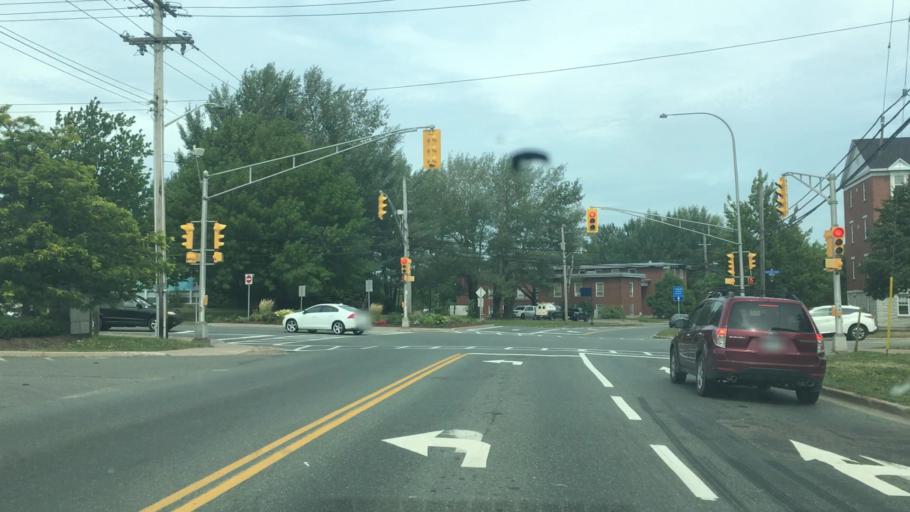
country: CA
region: Nova Scotia
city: Antigonish
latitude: 45.6162
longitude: -61.9990
